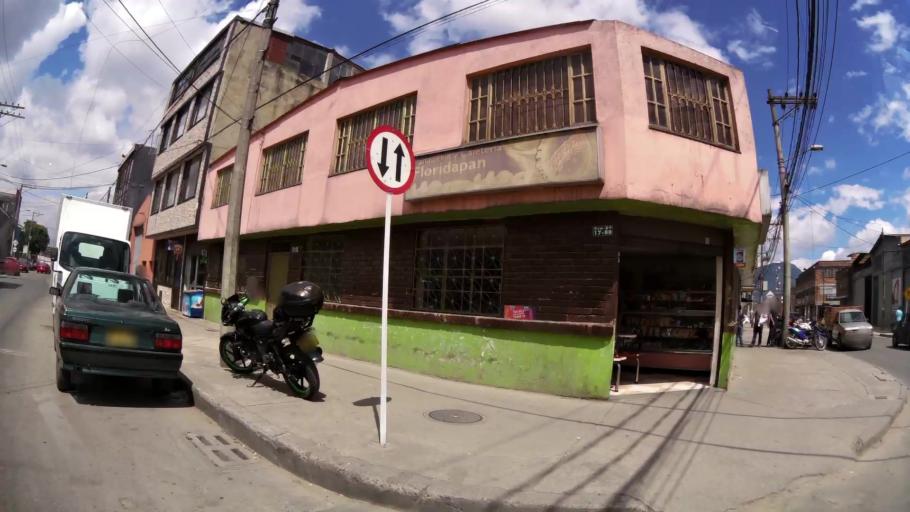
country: CO
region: Bogota D.C.
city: Bogota
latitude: 4.6338
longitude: -74.1099
